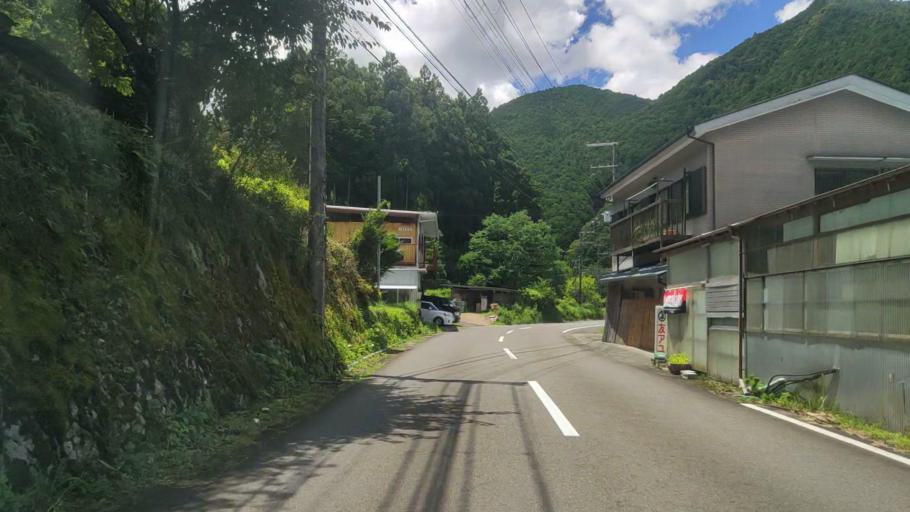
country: JP
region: Mie
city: Owase
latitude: 33.9601
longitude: 136.0650
